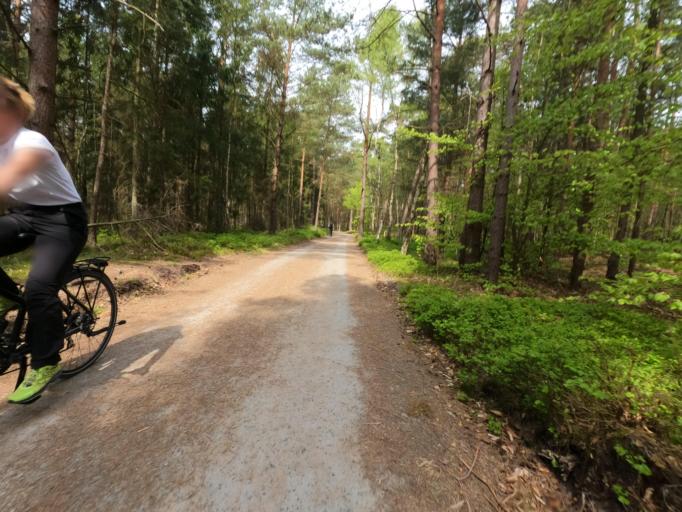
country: DE
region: Mecklenburg-Vorpommern
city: Ostseebad Prerow
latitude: 54.4525
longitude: 12.5169
